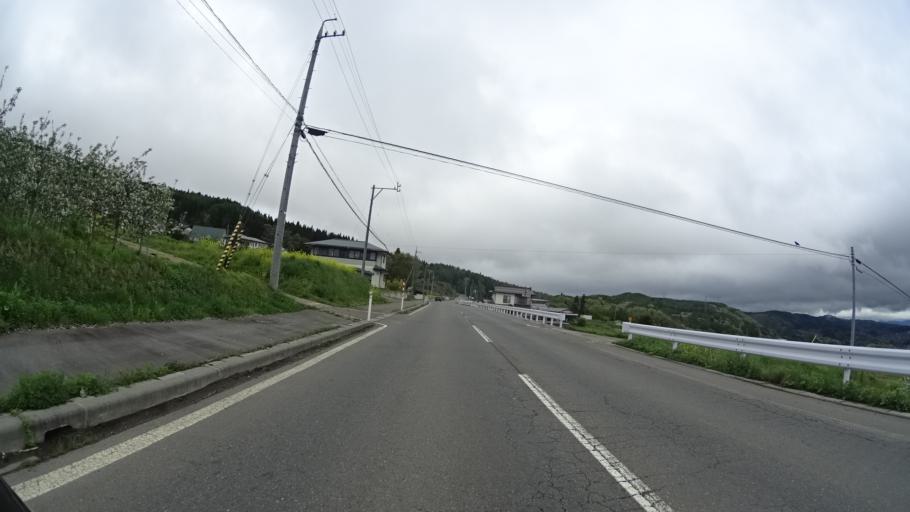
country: JP
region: Nagano
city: Nagano-shi
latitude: 36.7436
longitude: 138.2054
